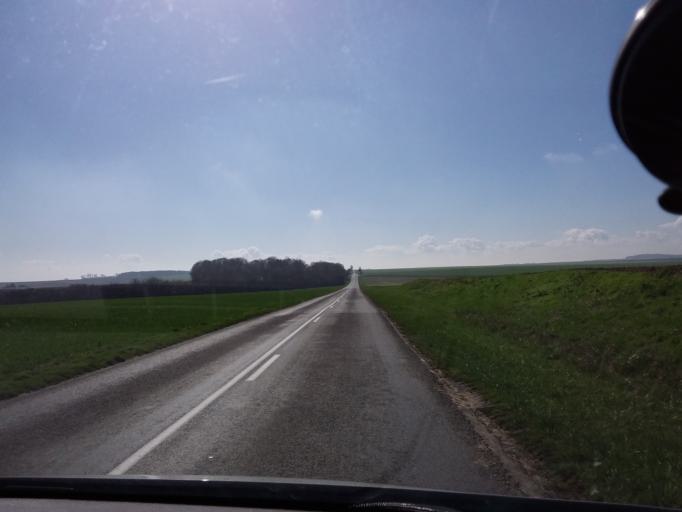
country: FR
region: Picardie
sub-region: Departement de l'Aisne
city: Guignicourt
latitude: 49.5042
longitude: 4.0403
